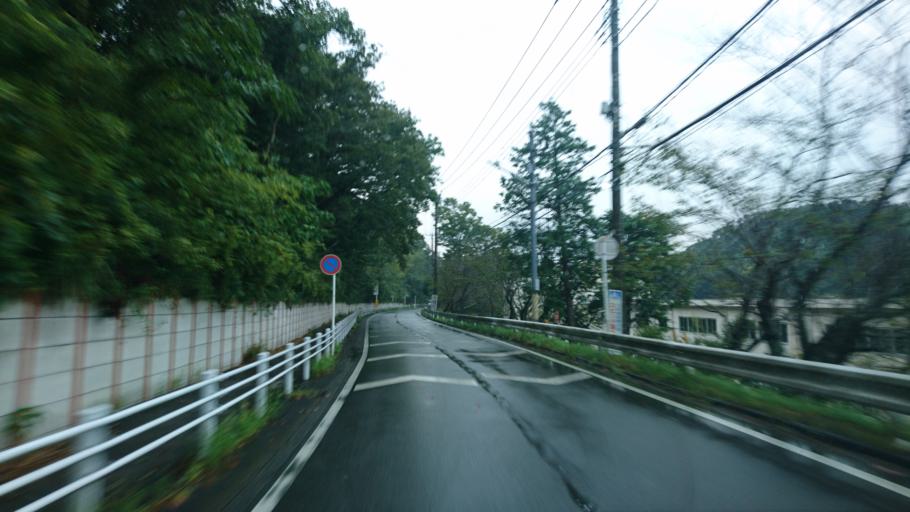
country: JP
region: Chiba
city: Kisarazu
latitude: 35.3431
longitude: 139.9215
